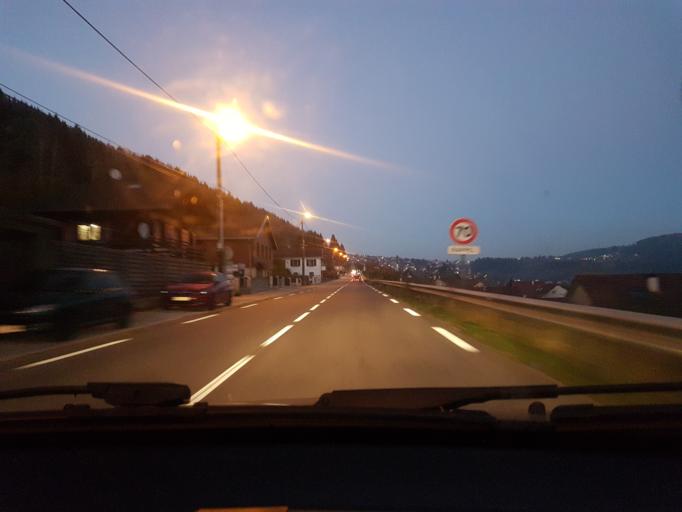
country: FR
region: Franche-Comte
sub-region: Departement du Doubs
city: Morteau
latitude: 47.0681
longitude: 6.6128
